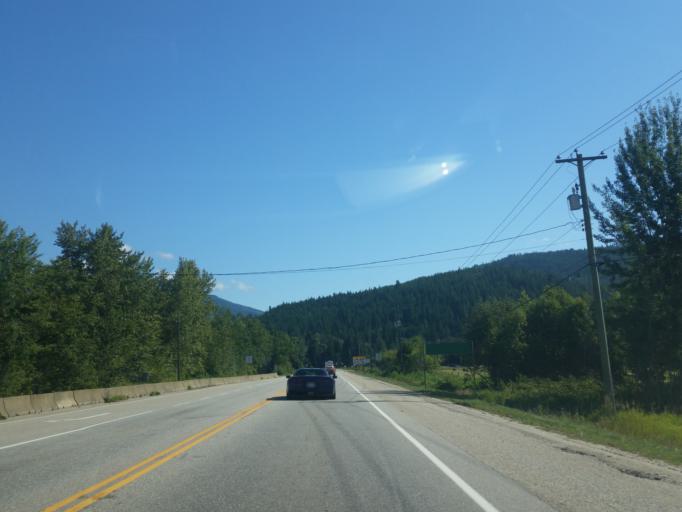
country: CA
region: British Columbia
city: Sicamous
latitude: 50.8470
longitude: -118.9520
